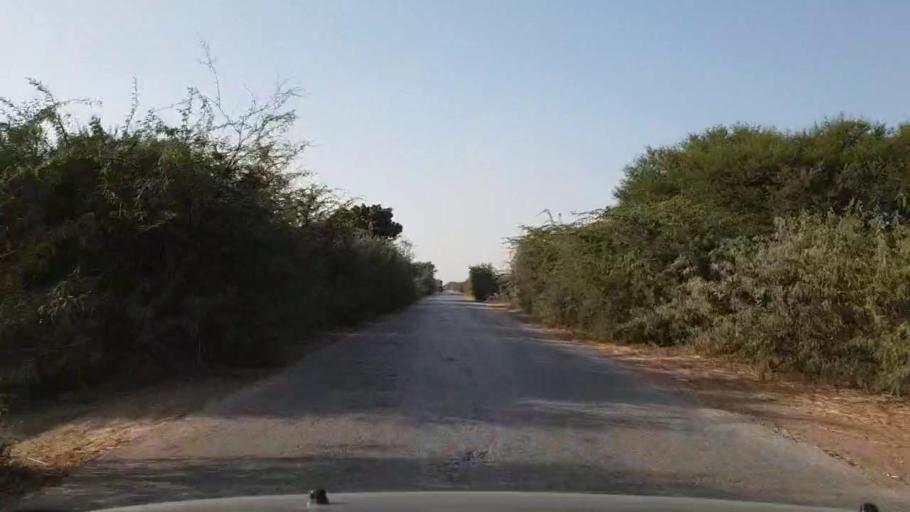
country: PK
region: Sindh
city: Tando Ghulam Ali
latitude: 25.1928
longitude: 68.8058
